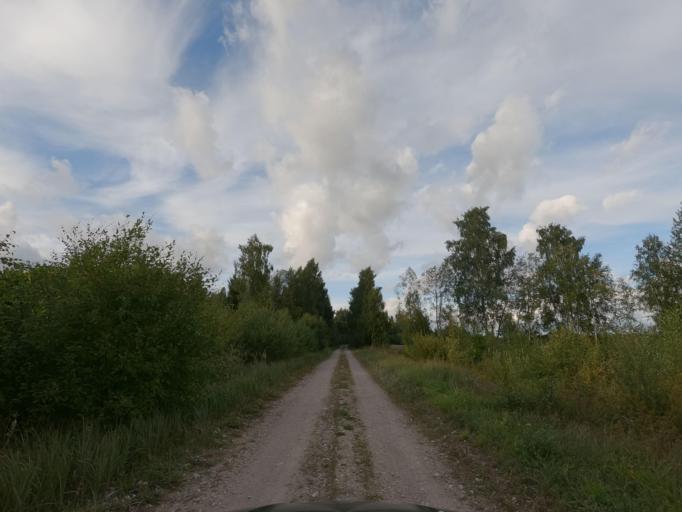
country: EE
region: Raplamaa
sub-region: Rapla vald
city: Rapla
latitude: 59.0113
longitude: 24.7611
